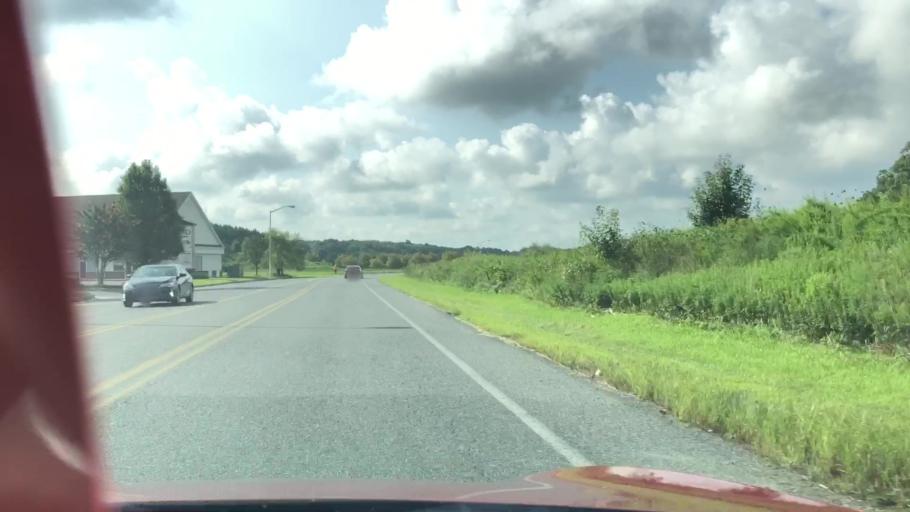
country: US
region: Maryland
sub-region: Wicomico County
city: Delmar
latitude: 38.4070
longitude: -75.5633
